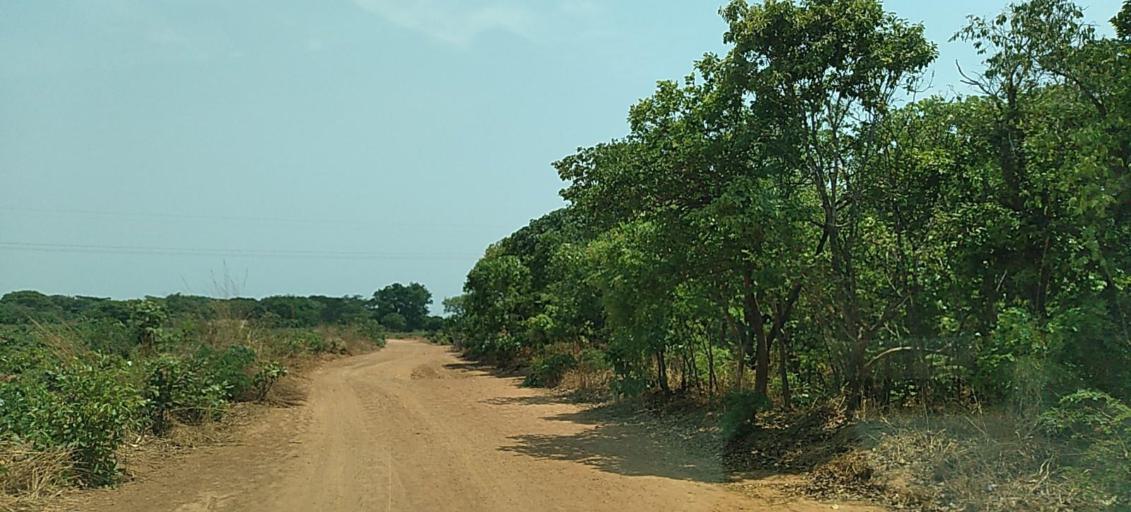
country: ZM
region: Copperbelt
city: Ndola
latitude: -13.0524
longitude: 28.7373
